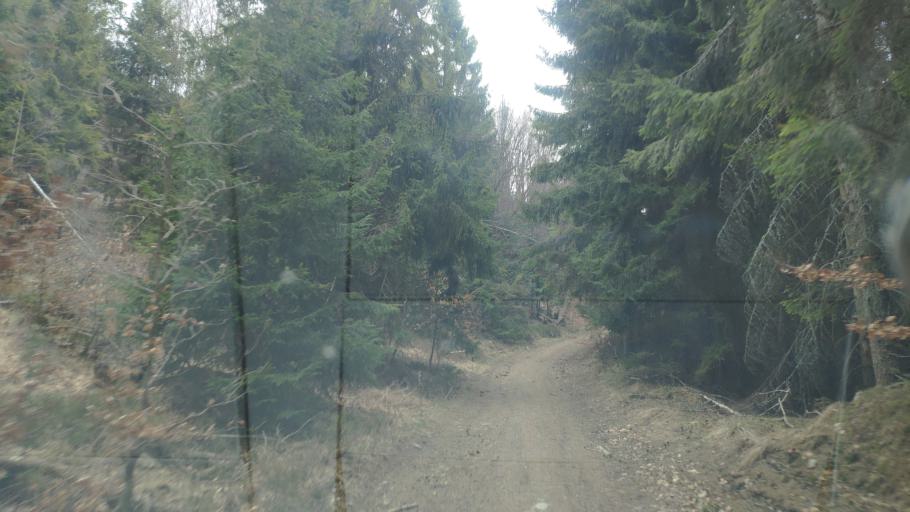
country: SK
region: Kosicky
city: Gelnica
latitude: 48.7627
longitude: 21.0294
